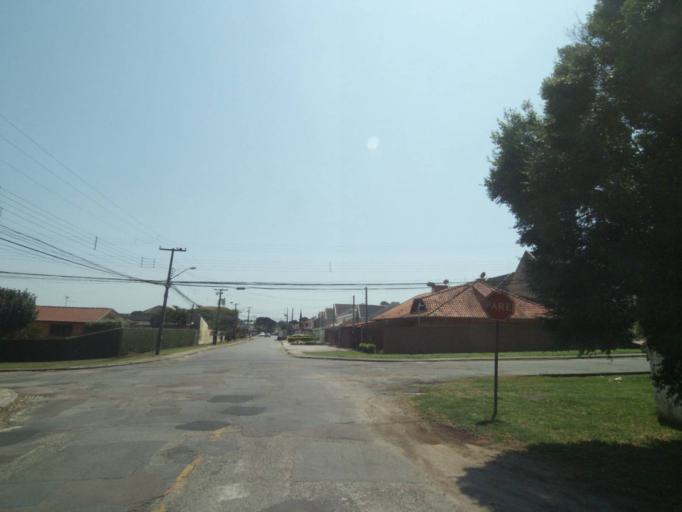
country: BR
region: Parana
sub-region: Sao Jose Dos Pinhais
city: Sao Jose dos Pinhais
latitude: -25.5172
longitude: -49.2639
